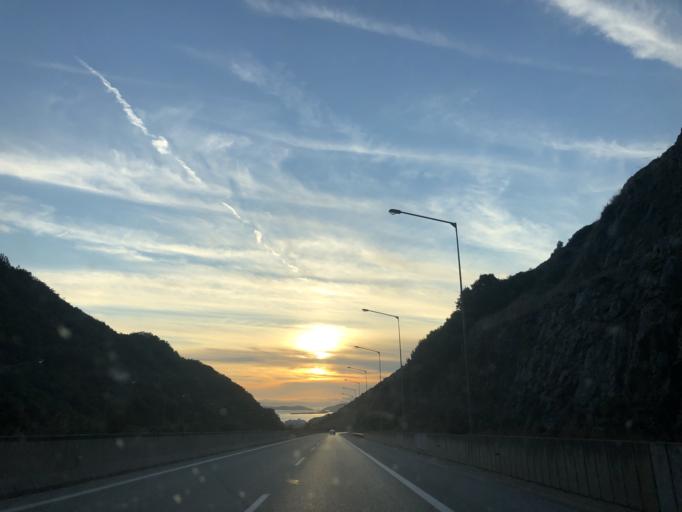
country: GR
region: Epirus
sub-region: Nomos Ioanninon
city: Pedini
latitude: 39.5669
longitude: 20.7531
